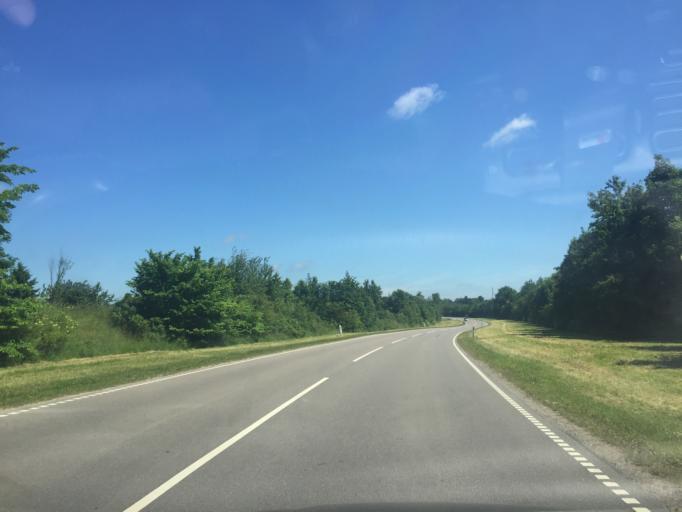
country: DK
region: Capital Region
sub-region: Hoje-Taastrup Kommune
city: Flong
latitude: 55.6613
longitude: 12.2002
